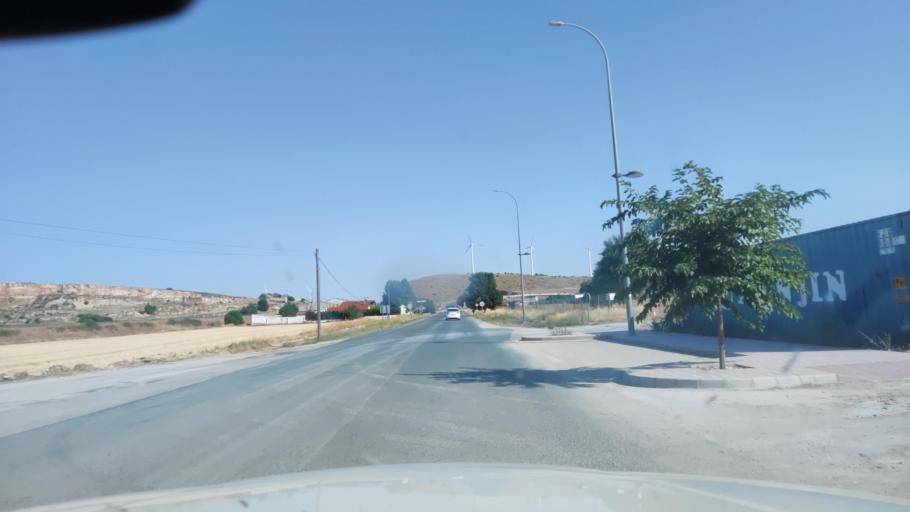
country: ES
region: Castille-La Mancha
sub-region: Provincia de Albacete
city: Pozo-Canada
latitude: 38.7982
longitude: -1.7286
